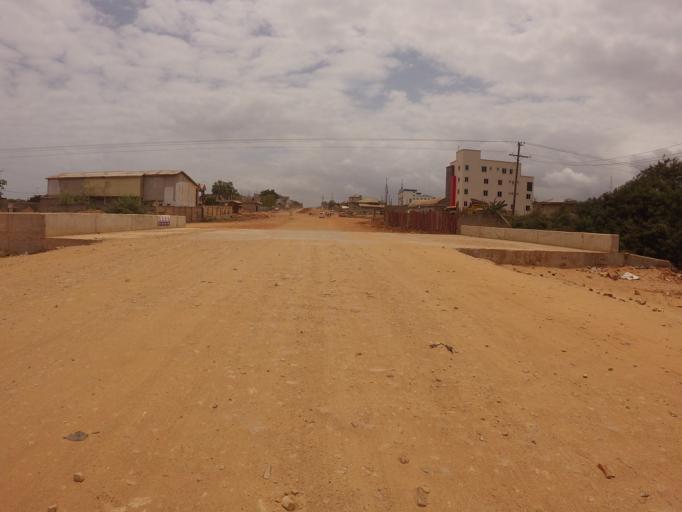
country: GH
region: Greater Accra
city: Medina Estates
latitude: 5.6305
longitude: -0.1392
